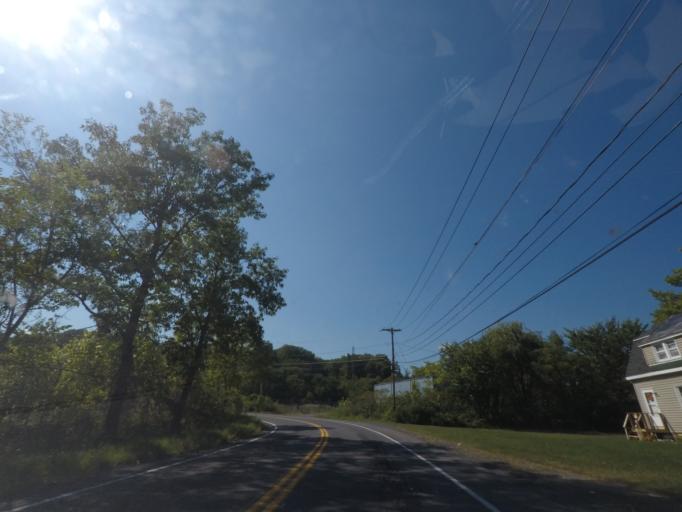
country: US
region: New York
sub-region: Albany County
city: Menands
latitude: 42.7152
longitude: -73.7219
